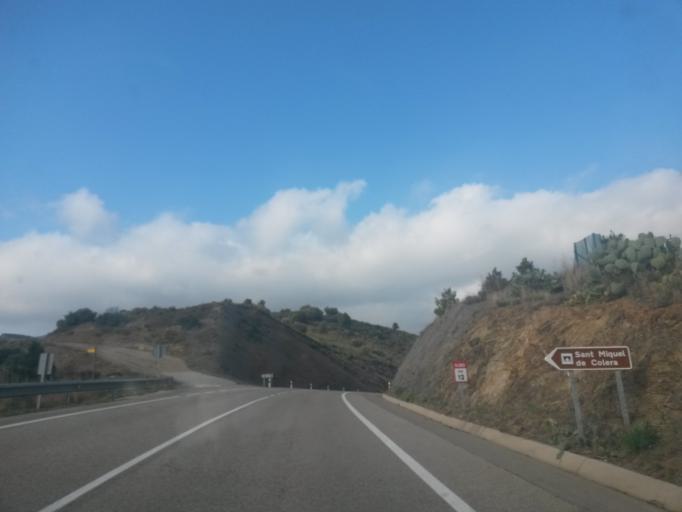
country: ES
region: Catalonia
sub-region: Provincia de Girona
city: Colera
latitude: 42.3989
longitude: 3.1510
